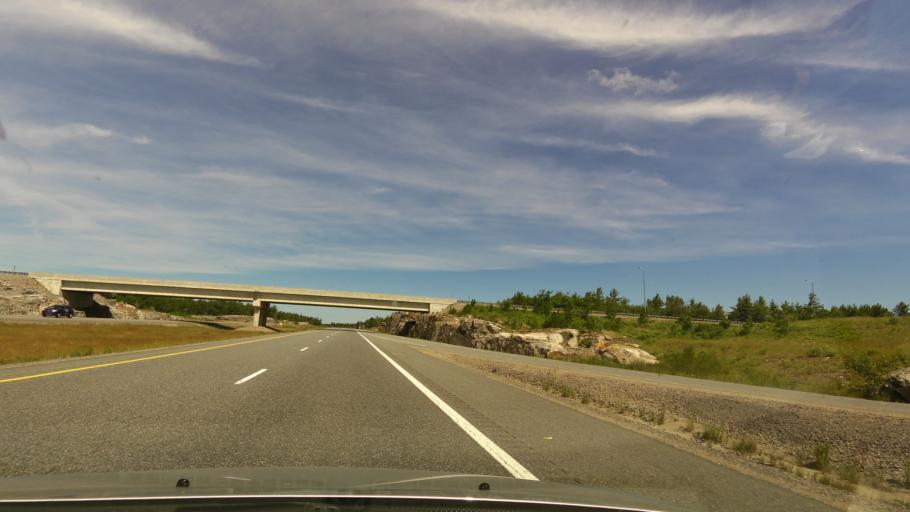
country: CA
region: Ontario
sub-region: Parry Sound District
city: Parry Sound
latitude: 45.4205
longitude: -80.0725
